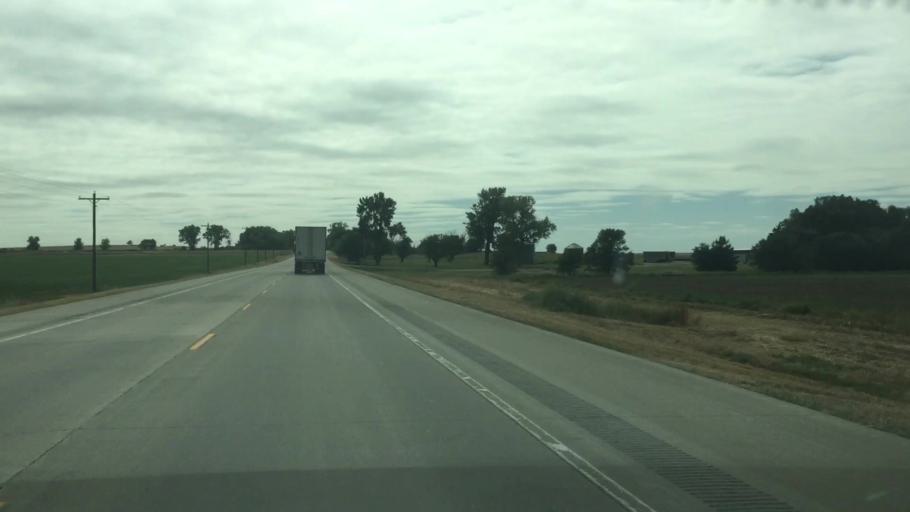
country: US
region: Colorado
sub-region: Prowers County
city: Lamar
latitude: 38.2158
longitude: -102.7242
